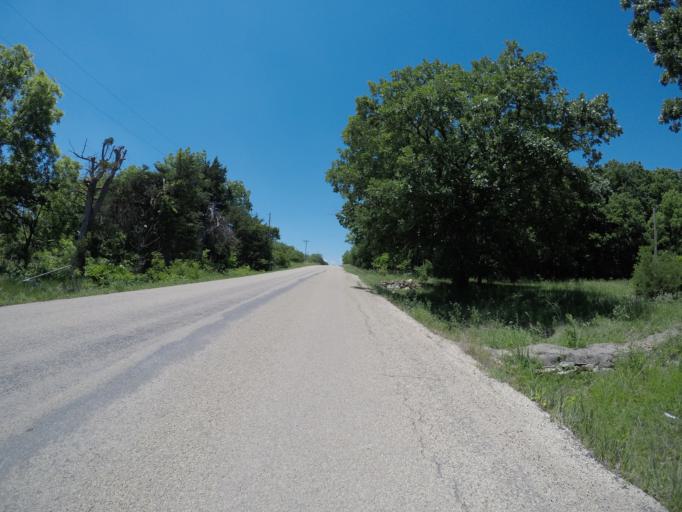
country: US
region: Kansas
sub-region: Geary County
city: Grandview Plaza
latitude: 38.8682
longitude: -96.7954
